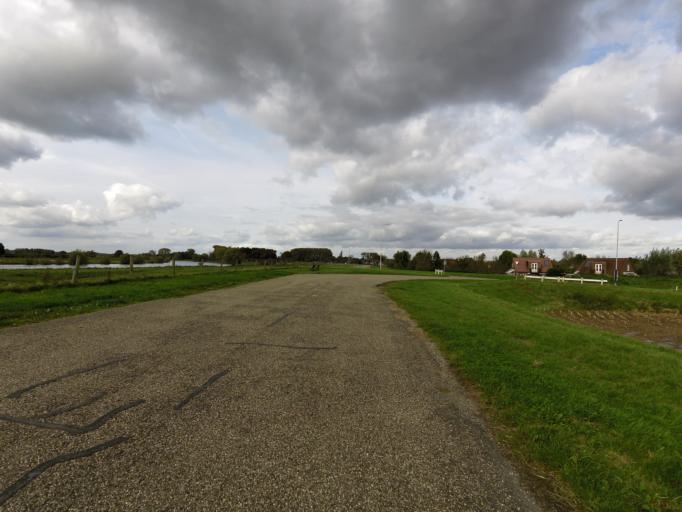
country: NL
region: Gelderland
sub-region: Gemeente Zutphen
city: Leesten
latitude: 52.1106
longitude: 6.2165
